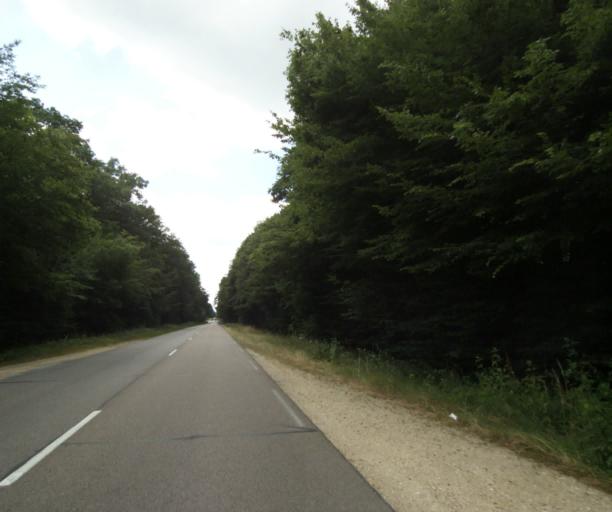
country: FR
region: Ile-de-France
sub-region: Departement de Seine-et-Marne
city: Thomery
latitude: 48.4204
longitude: 2.7984
